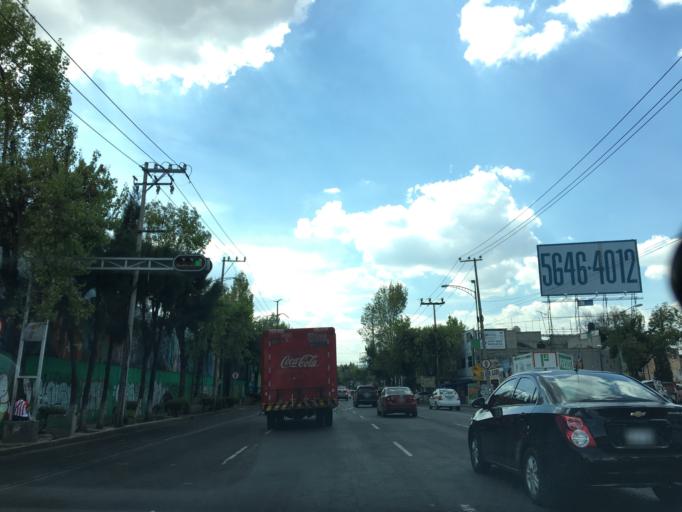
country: MX
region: Mexico City
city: Mexico City
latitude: 19.4090
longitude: -99.1277
